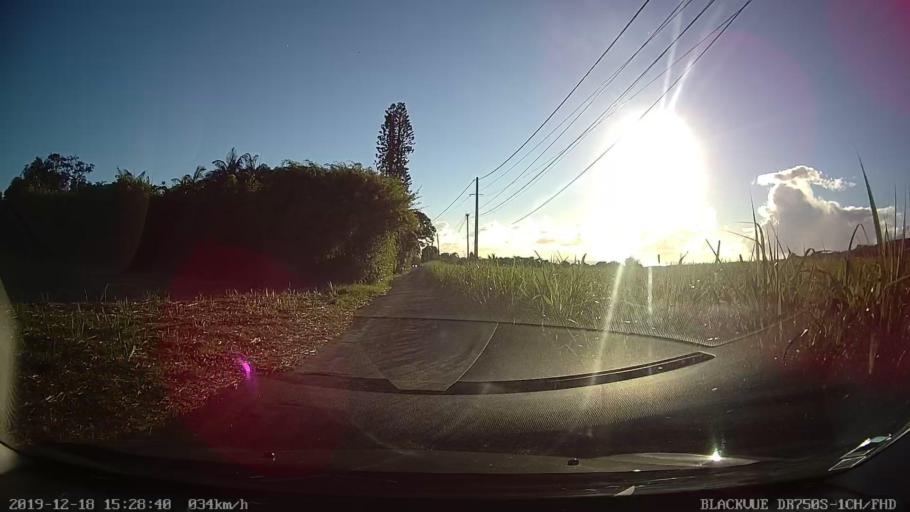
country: RE
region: Reunion
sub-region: Reunion
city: Bras-Panon
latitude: -20.9988
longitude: 55.6579
